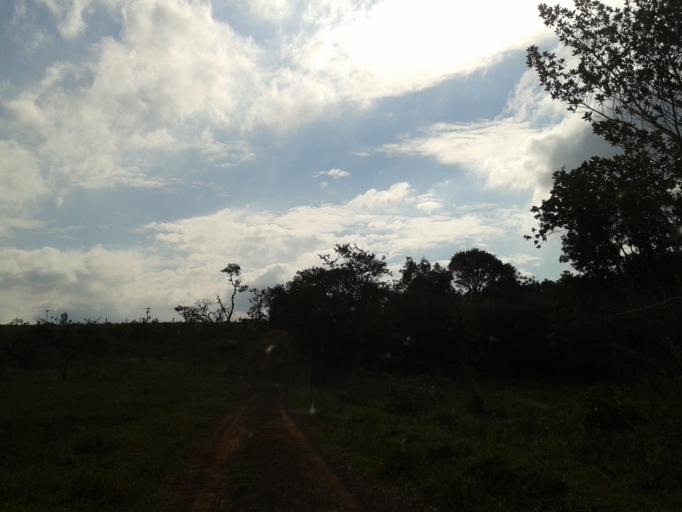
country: BR
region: Minas Gerais
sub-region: Campina Verde
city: Campina Verde
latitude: -19.3911
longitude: -49.6969
